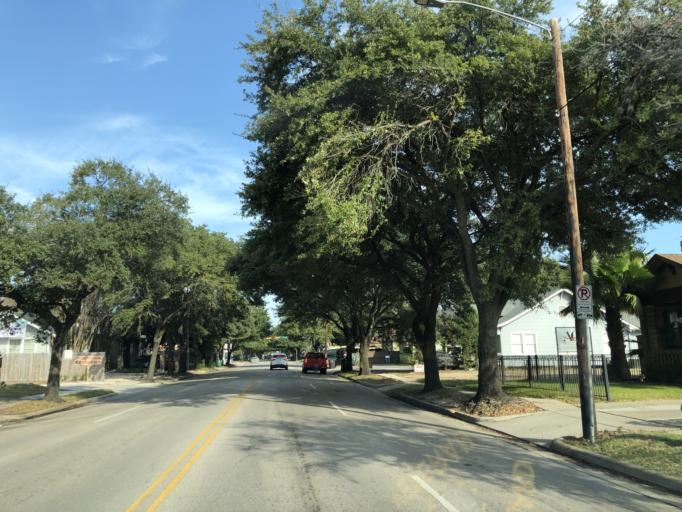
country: US
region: Texas
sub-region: Harris County
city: Houston
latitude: 29.7950
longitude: -95.3990
